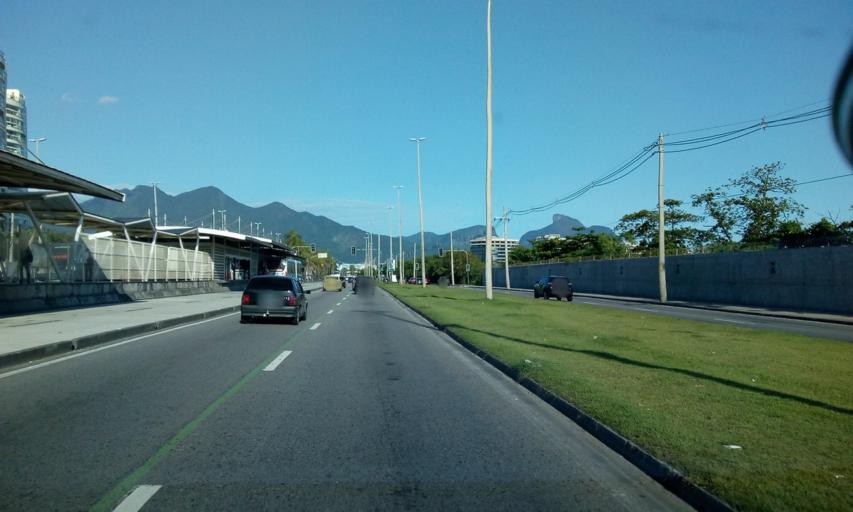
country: BR
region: Rio de Janeiro
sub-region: Nilopolis
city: Nilopolis
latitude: -22.9734
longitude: -43.3832
